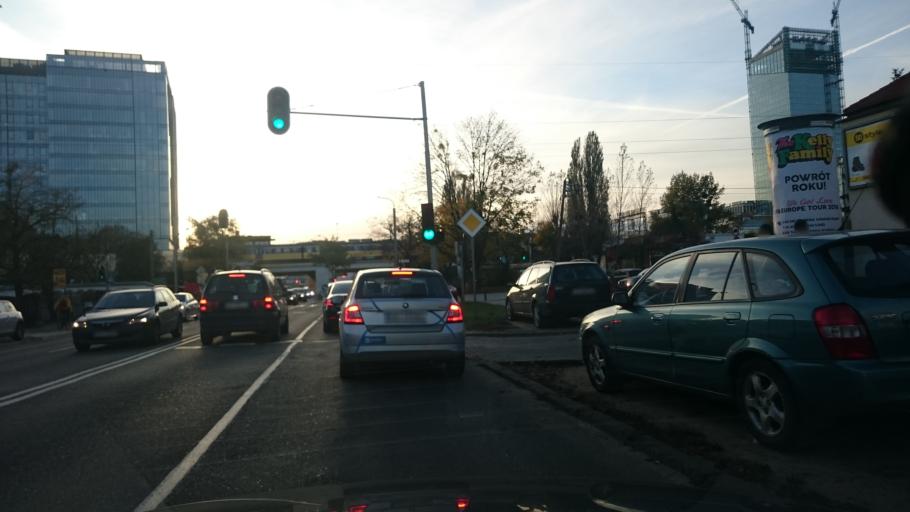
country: PL
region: Pomeranian Voivodeship
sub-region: Sopot
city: Sopot
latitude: 54.4018
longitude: 18.5780
